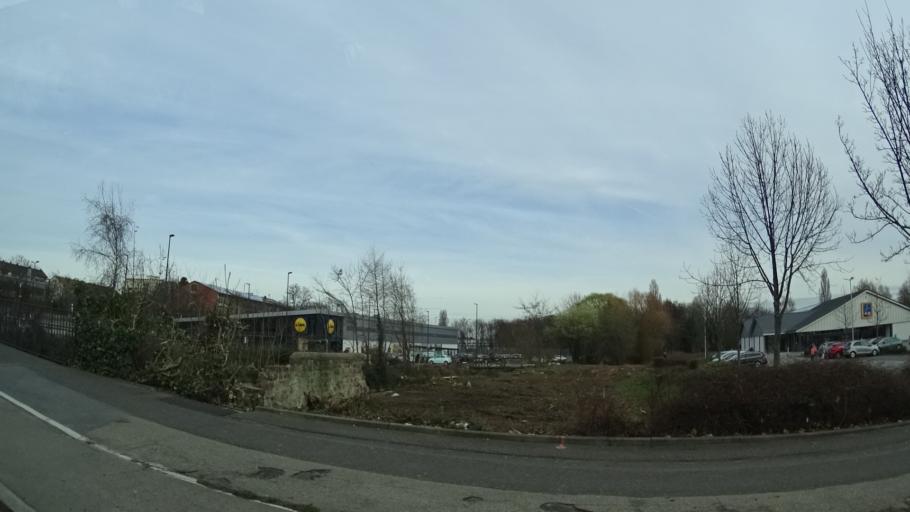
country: DE
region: Rheinland-Pfalz
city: Neustadt
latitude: 49.3557
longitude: 8.1520
